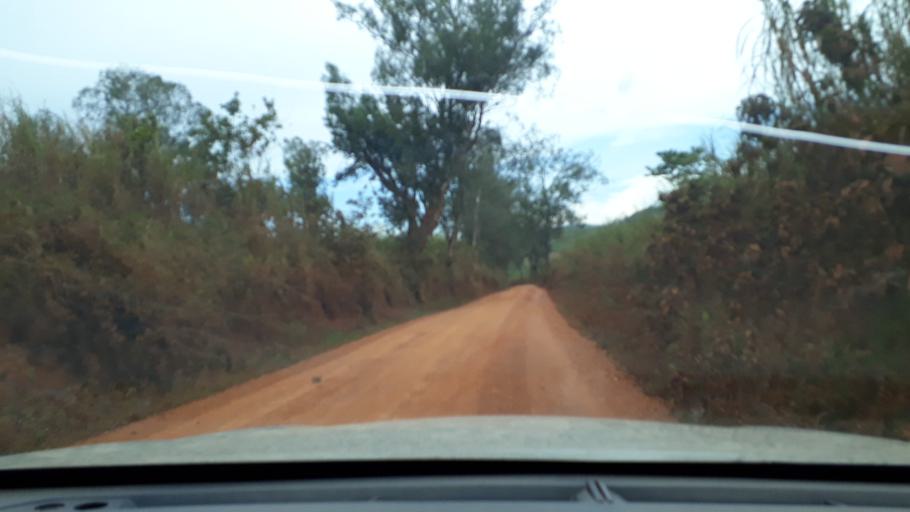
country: CD
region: Eastern Province
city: Bunia
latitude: 1.8318
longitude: 30.4527
